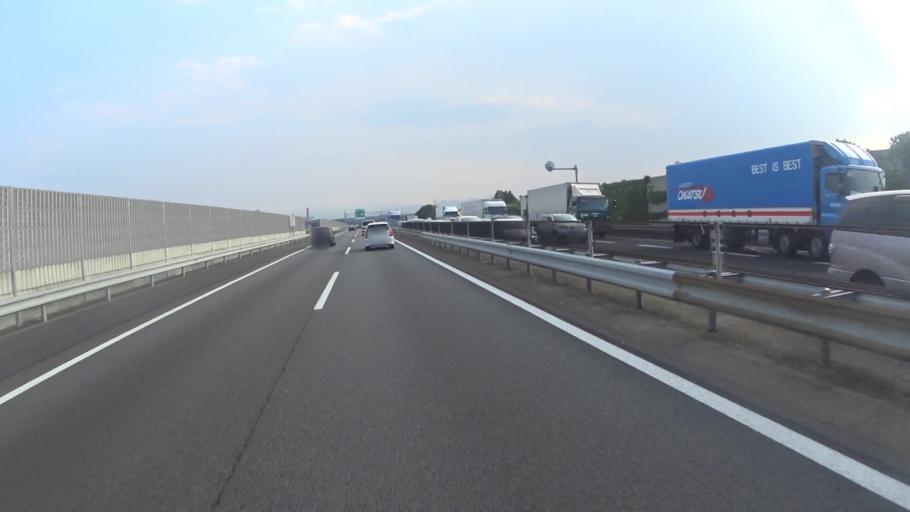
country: JP
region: Mie
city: Kameyama
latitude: 34.9137
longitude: 136.4777
